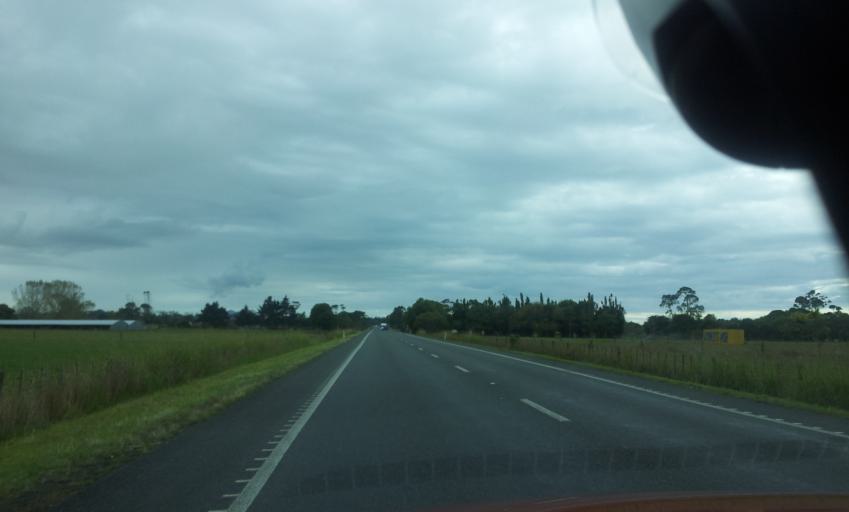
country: NZ
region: Northland
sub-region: Whangarei
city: Ruakaka
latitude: -35.9758
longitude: 174.4371
